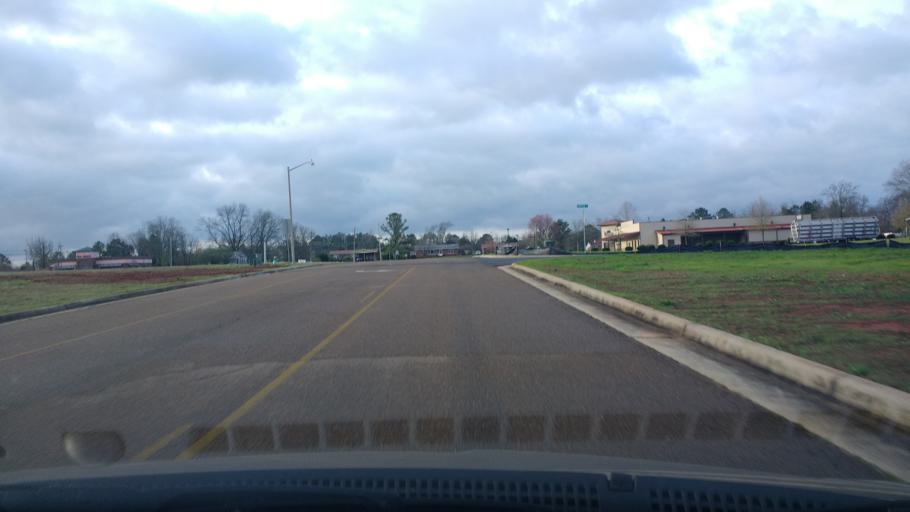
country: US
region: Alabama
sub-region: Madison County
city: Madison
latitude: 34.7087
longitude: -86.7452
